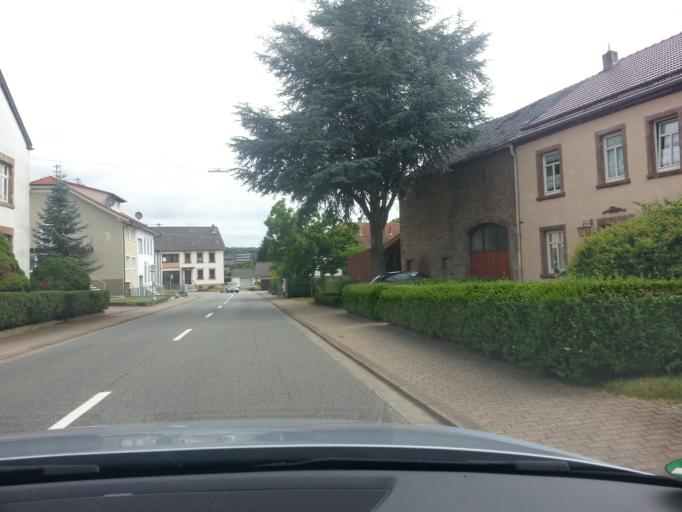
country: DE
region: Saarland
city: Losheim
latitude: 49.5006
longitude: 6.7762
